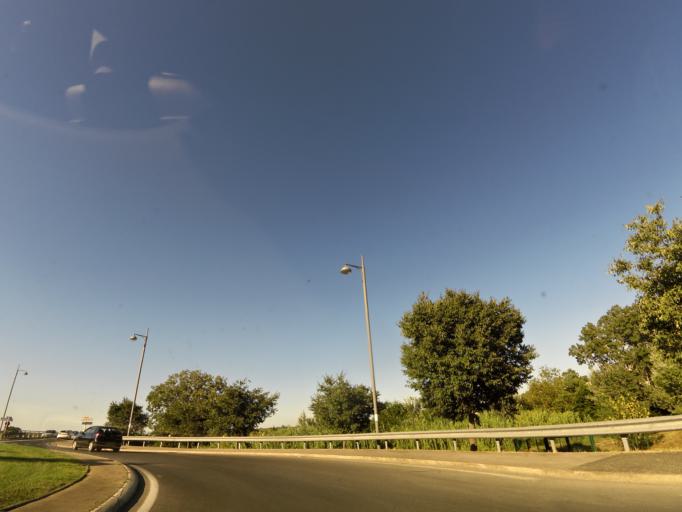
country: FR
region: Languedoc-Roussillon
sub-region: Departement du Gard
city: Sommieres
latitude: 43.7887
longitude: 4.0821
